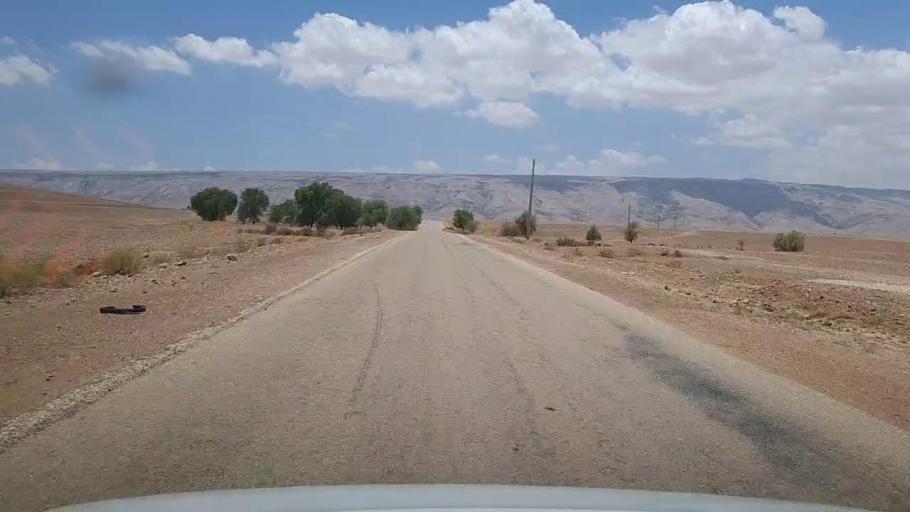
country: PK
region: Sindh
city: Bhan
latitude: 26.3202
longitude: 67.5491
